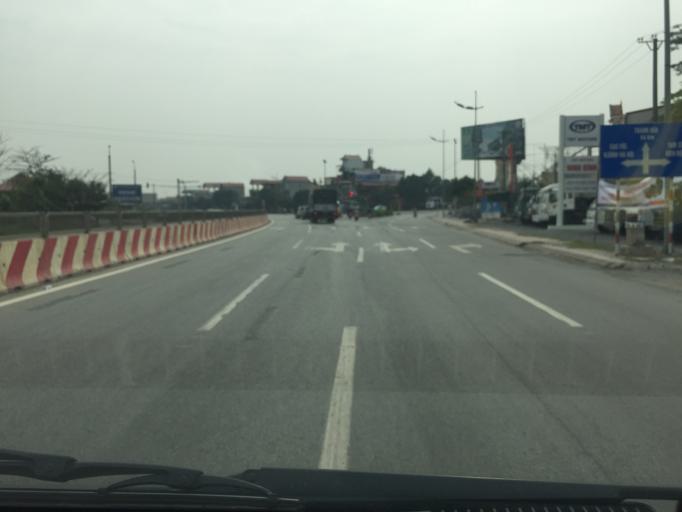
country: VN
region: Ninh Binh
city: Thanh Pho Ninh Binh
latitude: 20.2192
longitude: 105.9647
